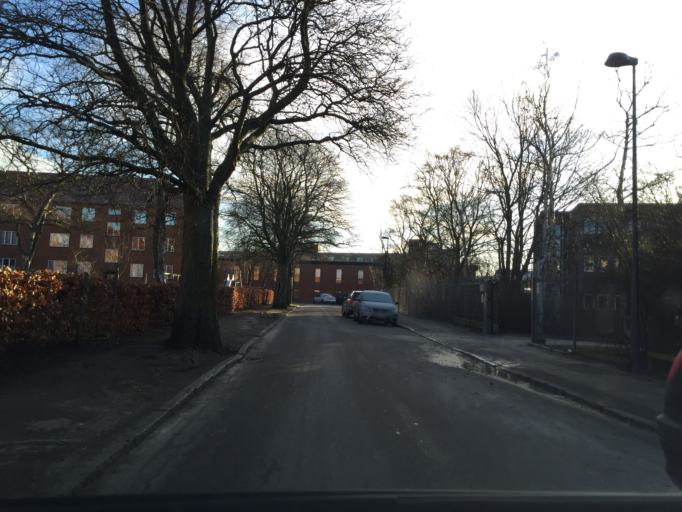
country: DK
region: Capital Region
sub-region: Kobenhavn
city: Vanlose
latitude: 55.6598
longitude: 12.5062
